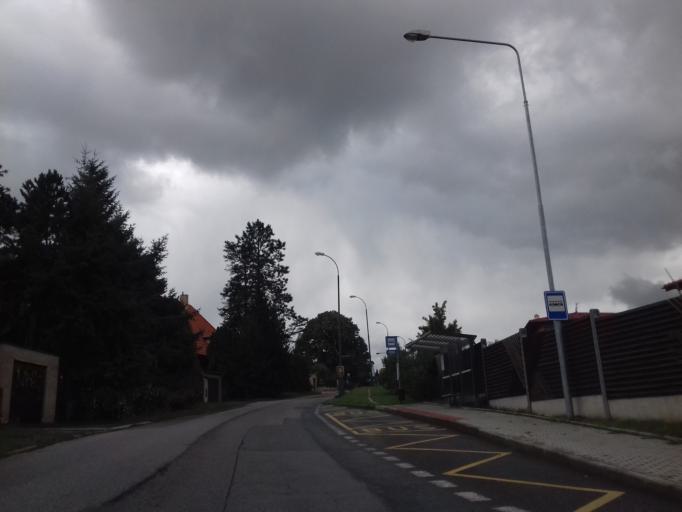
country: CZ
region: Central Bohemia
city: Cernosice
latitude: 49.9538
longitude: 14.3198
